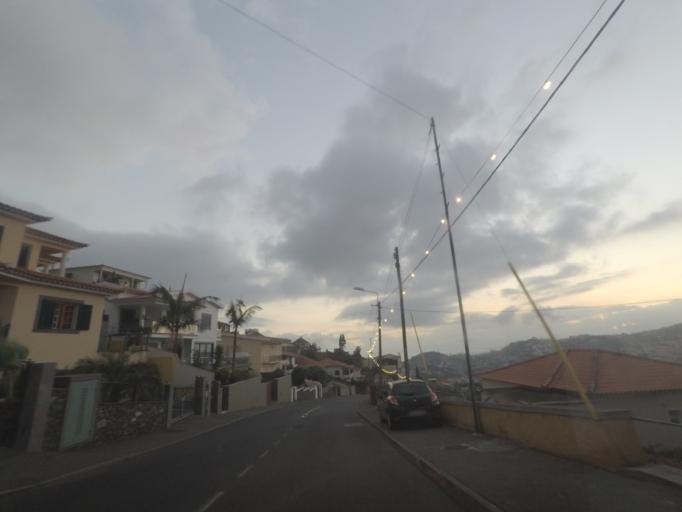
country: PT
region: Madeira
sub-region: Funchal
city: Nossa Senhora do Monte
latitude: 32.6709
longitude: -16.9228
